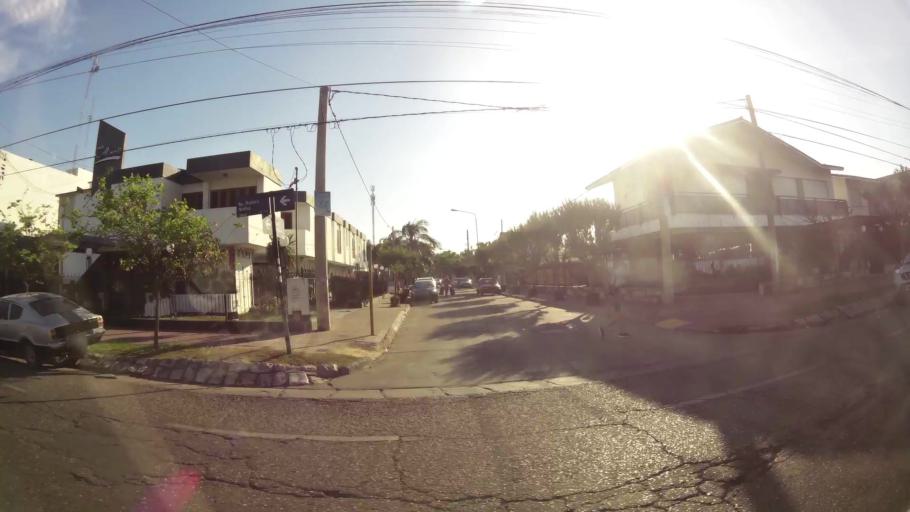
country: AR
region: Cordoba
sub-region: Departamento de Capital
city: Cordoba
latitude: -31.3747
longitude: -64.2279
